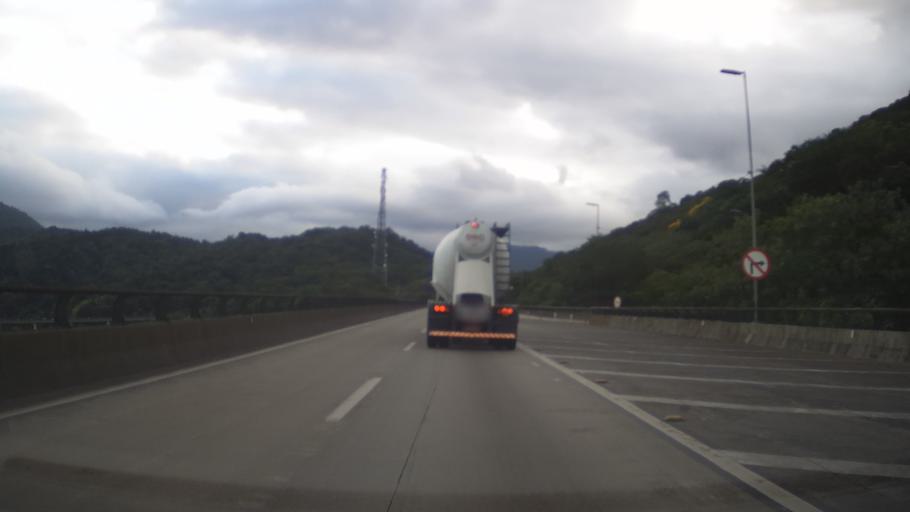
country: BR
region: Sao Paulo
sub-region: Cubatao
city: Cubatao
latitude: -23.9022
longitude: -46.4567
